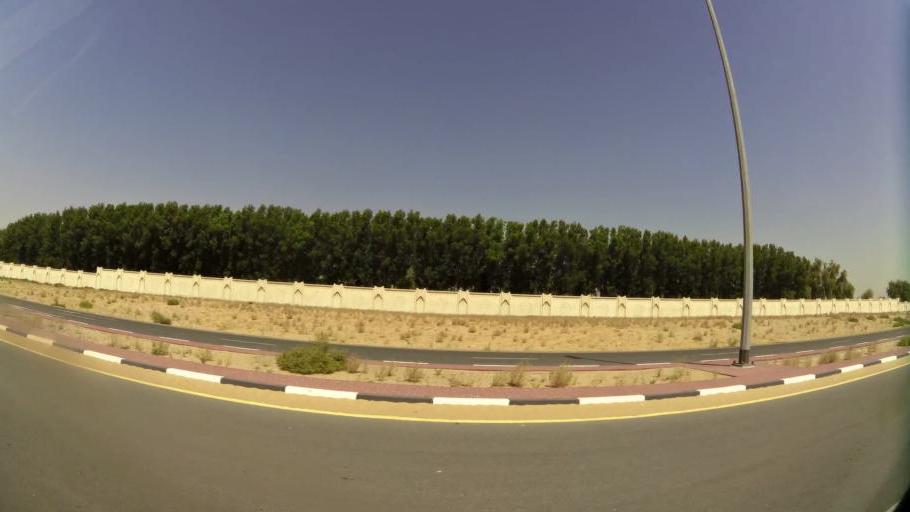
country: AE
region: Ajman
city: Ajman
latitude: 25.3993
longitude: 55.5374
